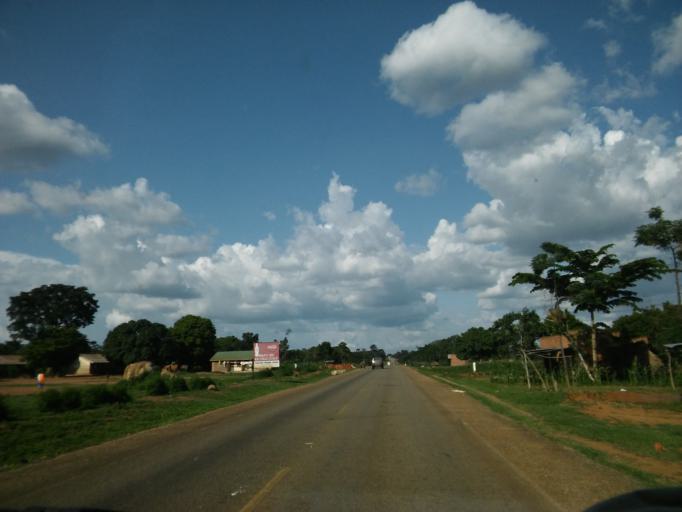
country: UG
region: Eastern Region
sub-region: Kibuku District
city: Kibuku
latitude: 1.0140
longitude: 33.8303
